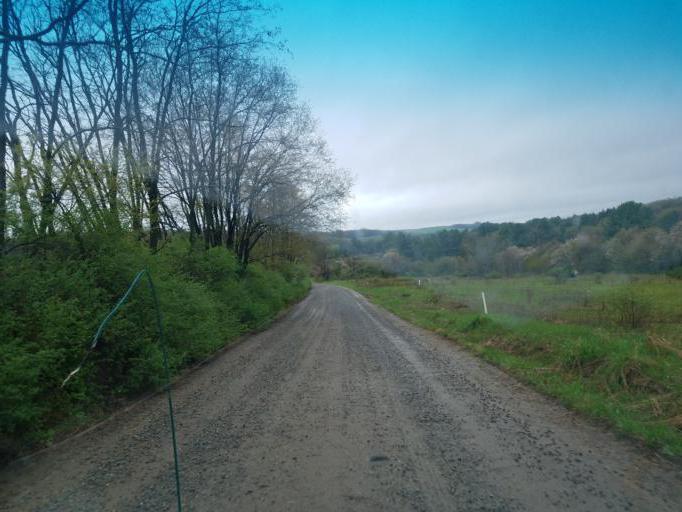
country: US
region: New York
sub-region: Allegany County
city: Andover
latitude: 41.9873
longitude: -77.7411
